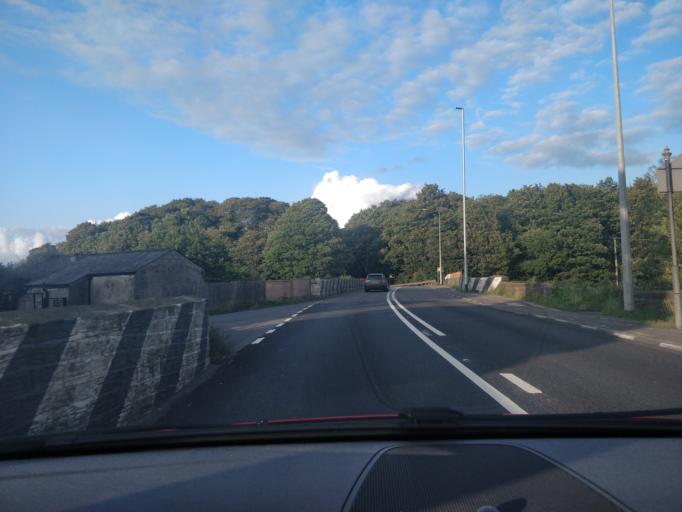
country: GB
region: England
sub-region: Lancashire
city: Tarleton
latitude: 53.6759
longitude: -2.8192
